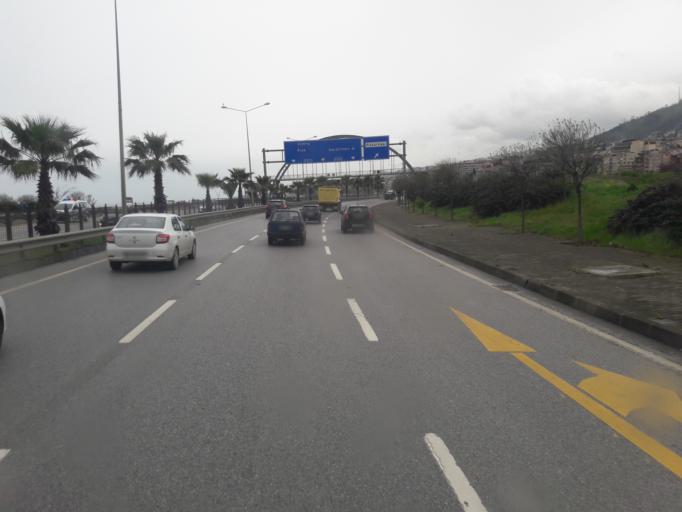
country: TR
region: Trabzon
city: Trabzon
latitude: 41.0120
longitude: 39.7217
